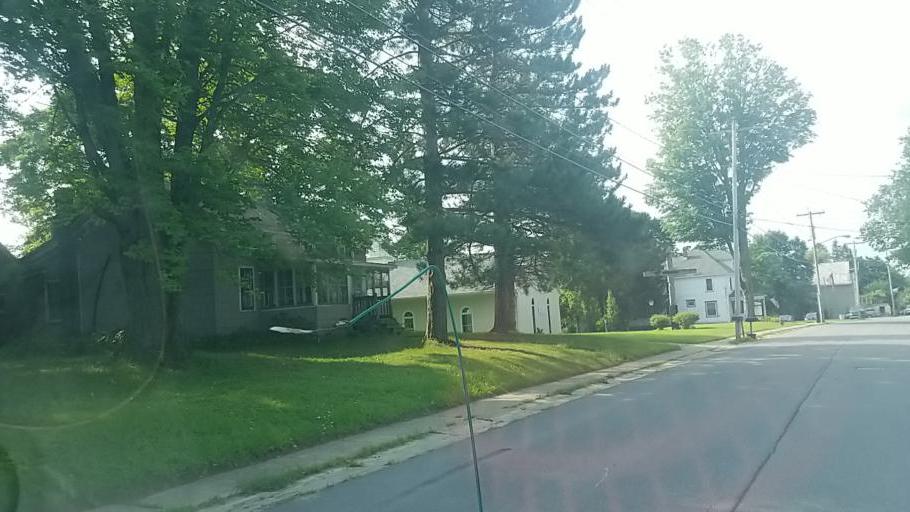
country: US
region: New York
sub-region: Fulton County
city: Broadalbin
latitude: 43.1061
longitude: -74.2632
